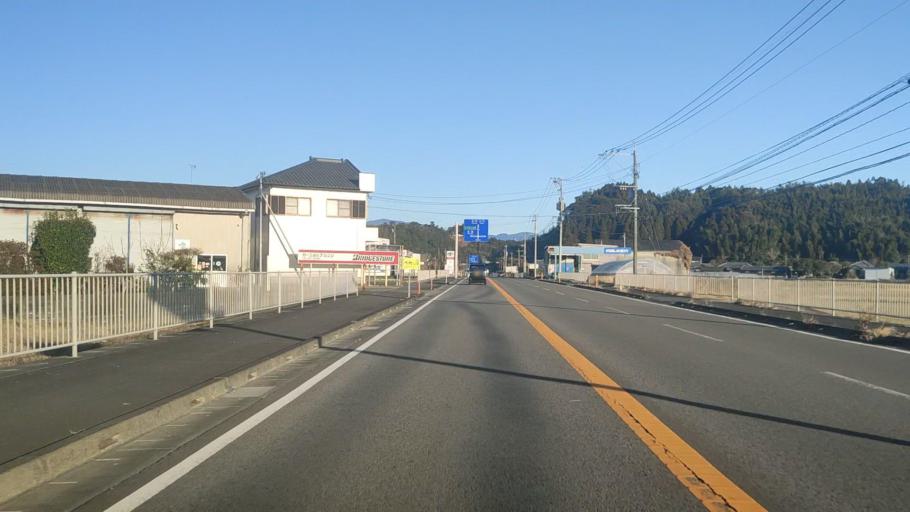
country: JP
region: Miyazaki
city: Takanabe
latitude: 32.1418
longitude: 131.5271
